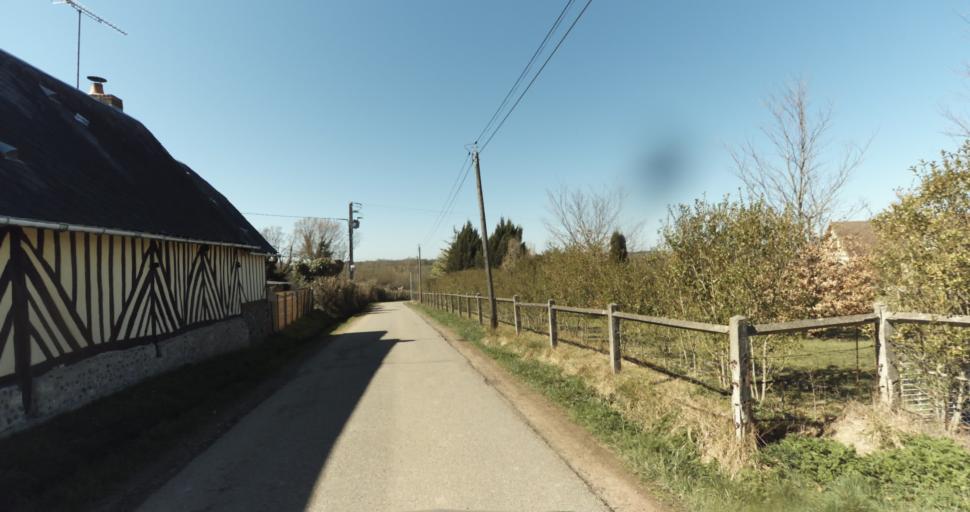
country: FR
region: Lower Normandy
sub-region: Departement du Calvados
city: Livarot
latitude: 48.9960
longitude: 0.1038
